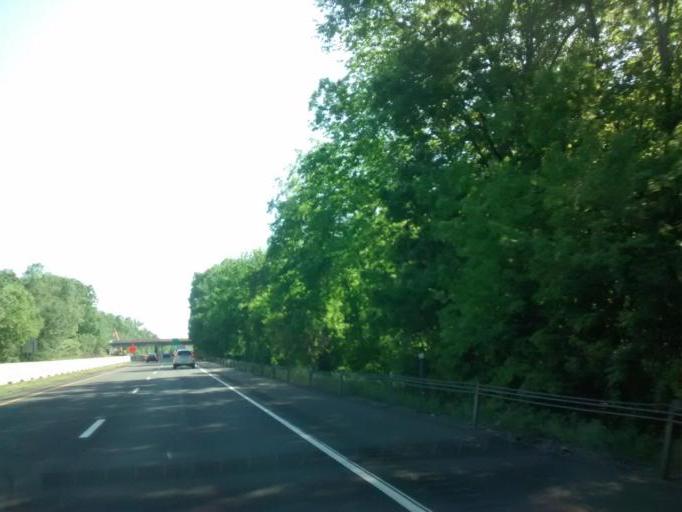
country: US
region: Connecticut
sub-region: New London County
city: Niantic
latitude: 41.3470
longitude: -72.2263
